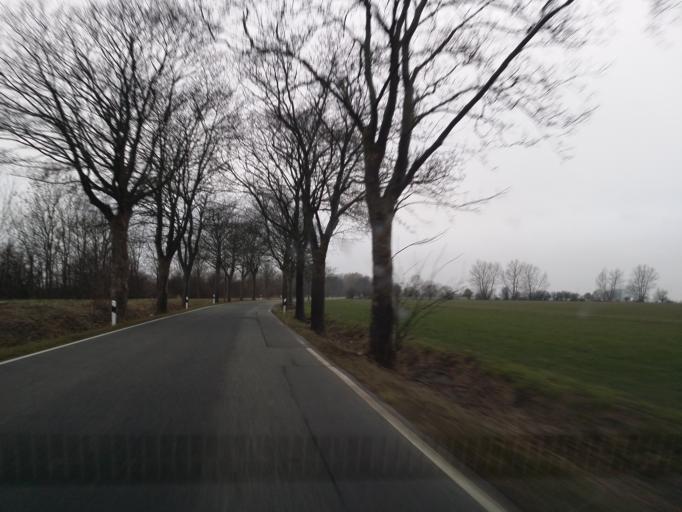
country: DE
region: Schleswig-Holstein
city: Fehmarn
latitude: 54.4591
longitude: 11.1267
